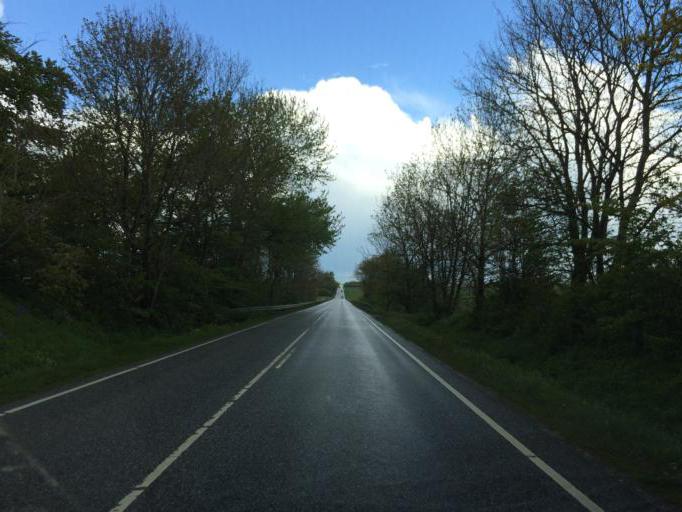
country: DK
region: Central Jutland
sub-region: Holstebro Kommune
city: Holstebro
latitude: 56.3924
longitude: 8.6629
